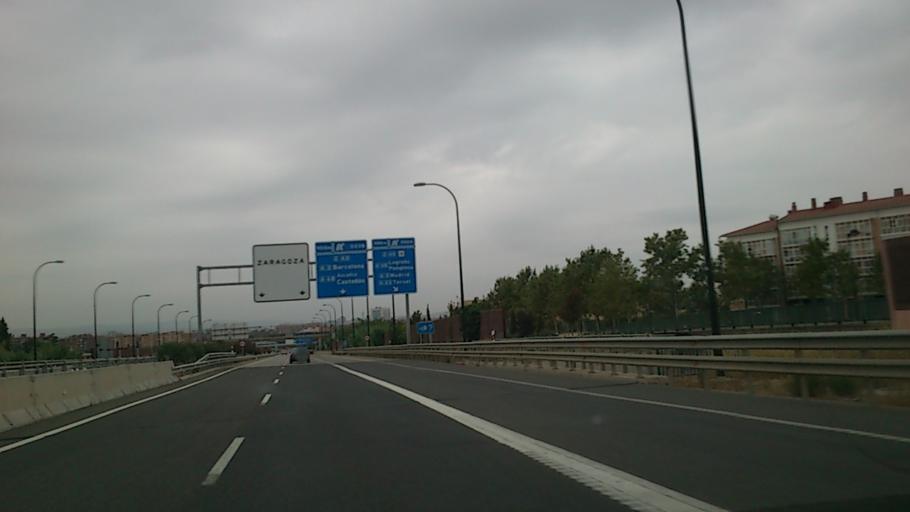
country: ES
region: Aragon
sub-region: Provincia de Zaragoza
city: Zaragoza
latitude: 41.6870
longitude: -0.8727
